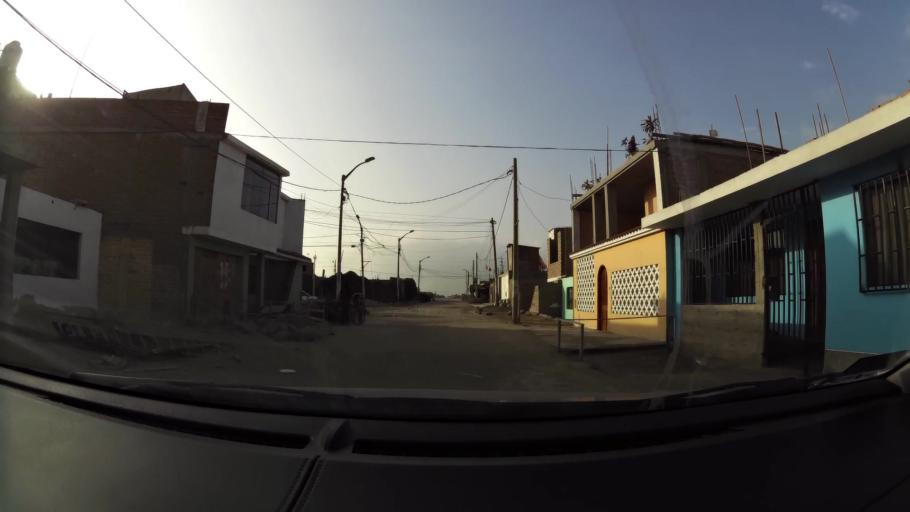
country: PE
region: Lima
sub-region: Lima
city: Santa Rosa
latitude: -11.7746
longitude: -77.1603
